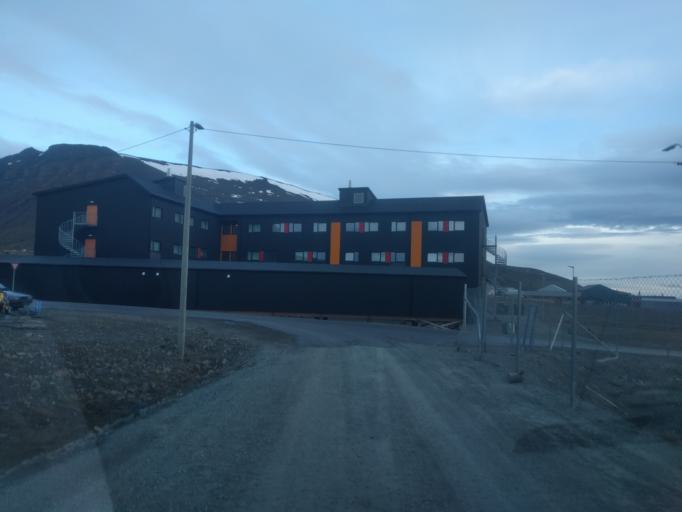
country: SJ
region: Svalbard
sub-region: Spitsbergen
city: Longyearbyen
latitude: 78.2236
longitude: 15.6512
